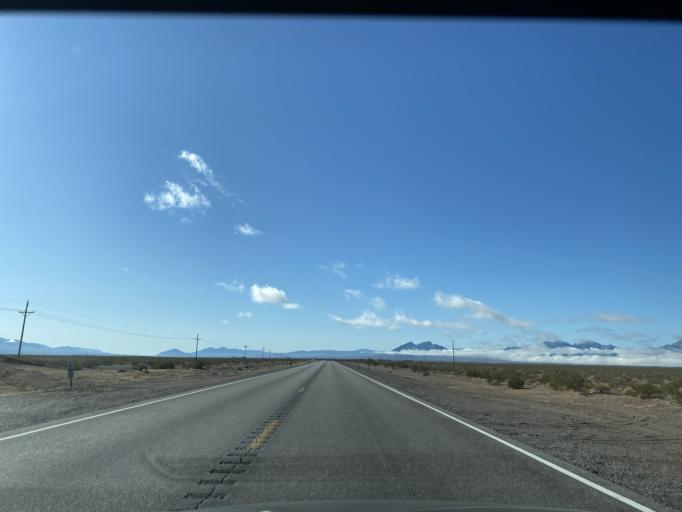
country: US
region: Nevada
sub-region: Nye County
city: Beatty
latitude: 36.5571
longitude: -116.4157
